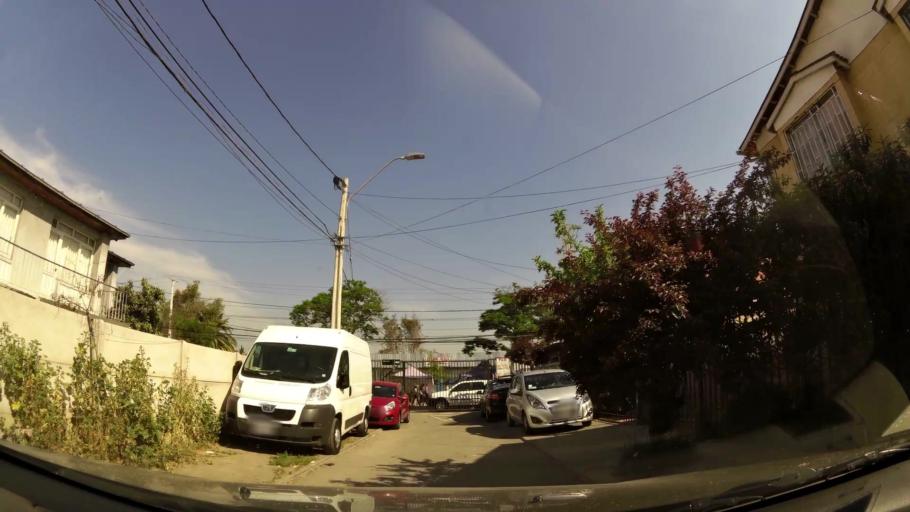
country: CL
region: Santiago Metropolitan
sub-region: Provincia de Maipo
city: San Bernardo
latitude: -33.5961
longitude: -70.6927
